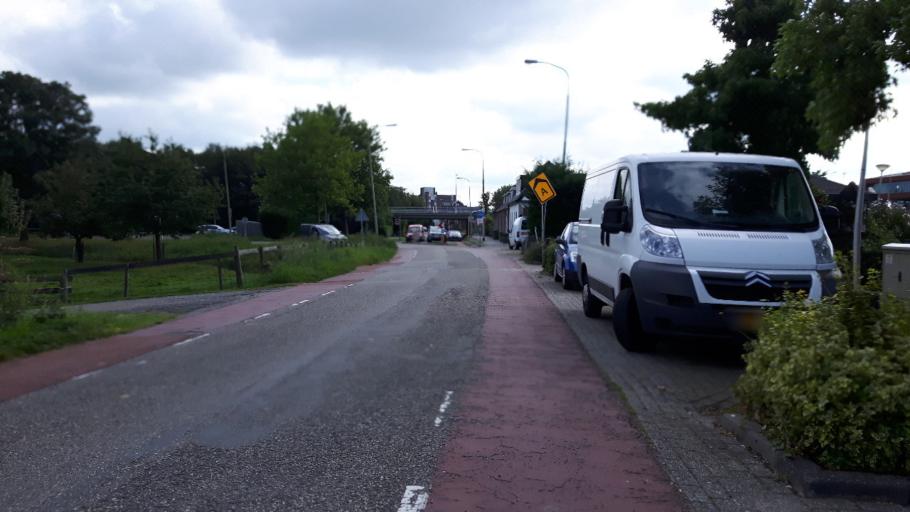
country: NL
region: South Holland
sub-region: Bodegraven-Reeuwijk
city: Bodegraven
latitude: 52.0904
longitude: 4.7396
